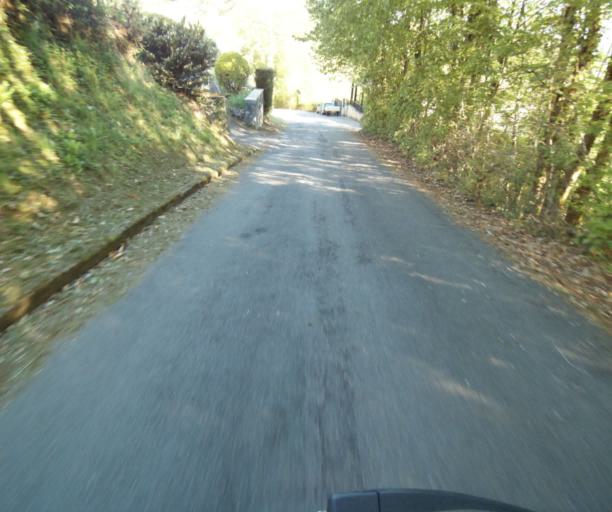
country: FR
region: Limousin
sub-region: Departement de la Correze
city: Tulle
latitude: 45.2609
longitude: 1.7680
